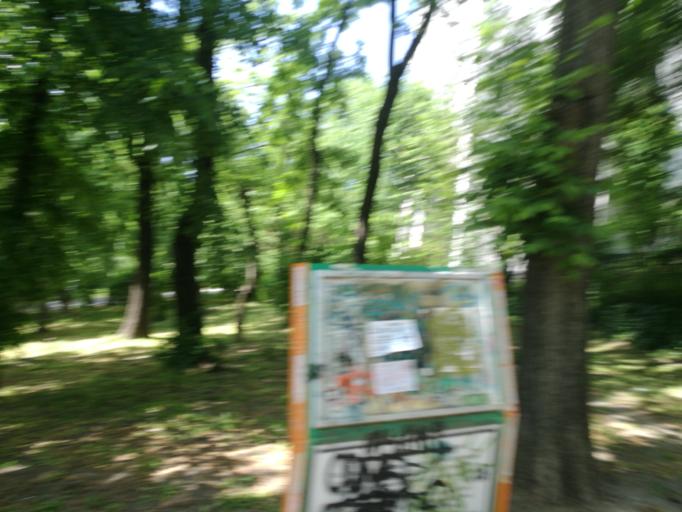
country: RO
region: Bucuresti
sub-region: Municipiul Bucuresti
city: Bucuresti
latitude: 44.4374
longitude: 26.0927
